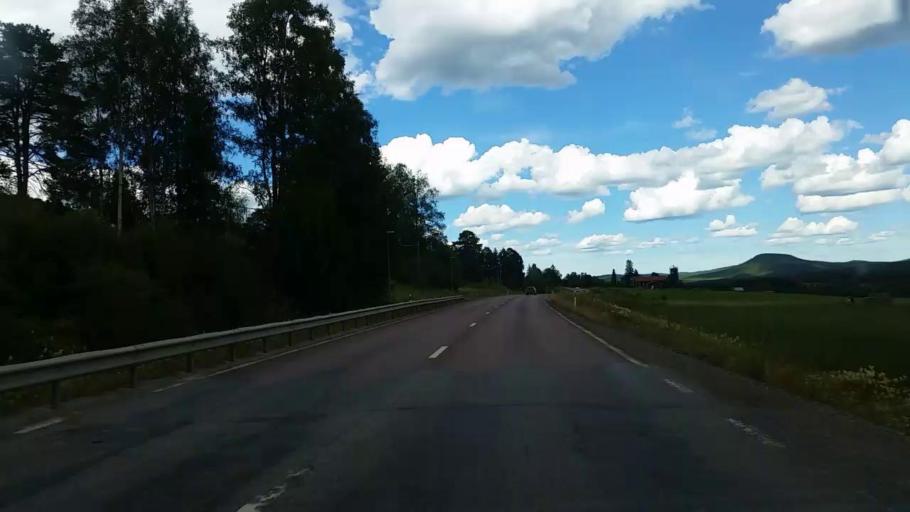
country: SE
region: Gaevleborg
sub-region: Ljusdals Kommun
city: Jaervsoe
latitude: 61.6934
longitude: 16.1548
